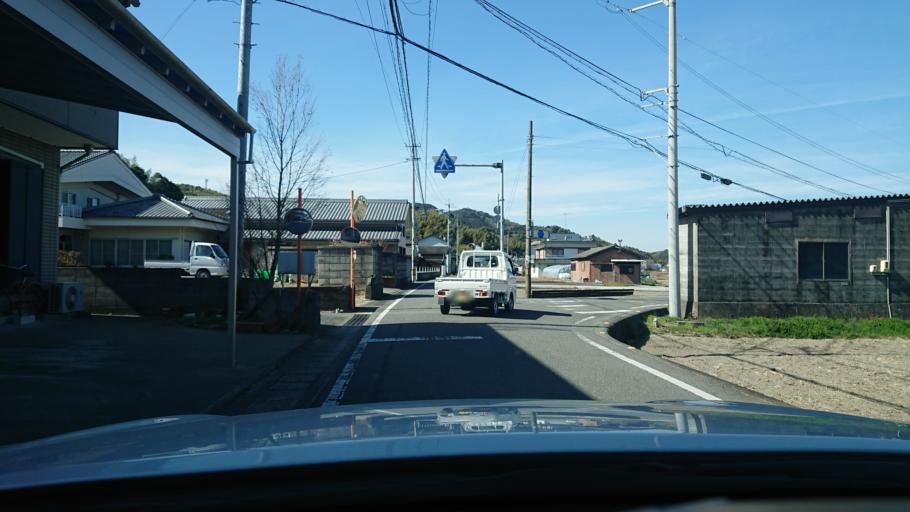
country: JP
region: Tokushima
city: Komatsushimacho
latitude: 33.9800
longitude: 134.5886
